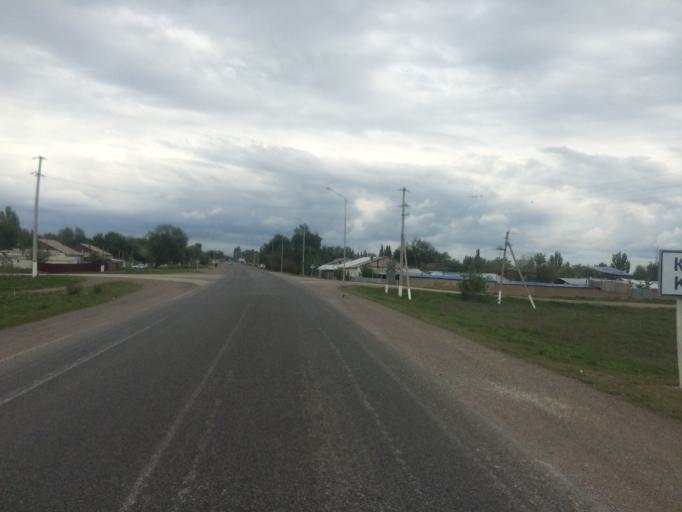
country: KZ
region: Zhambyl
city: Georgiyevka
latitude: 43.2281
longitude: 74.3859
